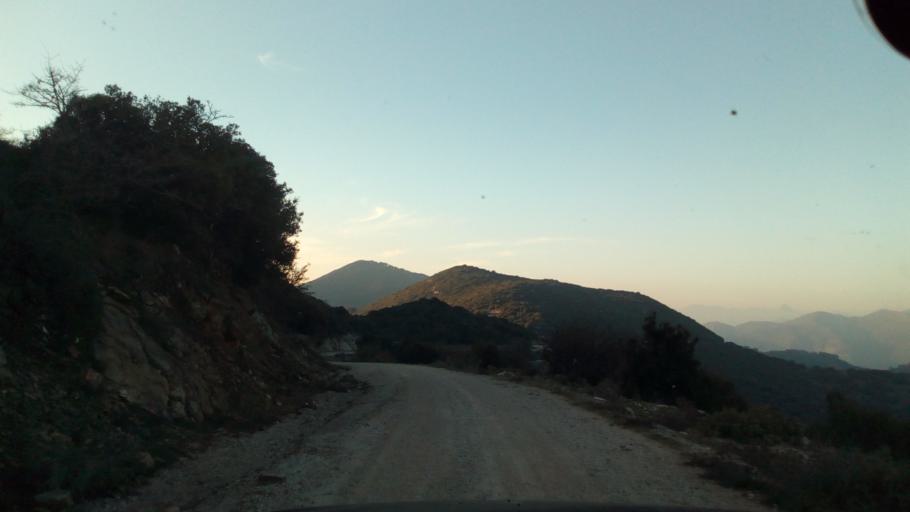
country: GR
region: West Greece
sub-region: Nomos Aitolias kai Akarnanias
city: Nafpaktos
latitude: 38.4651
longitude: 21.8274
